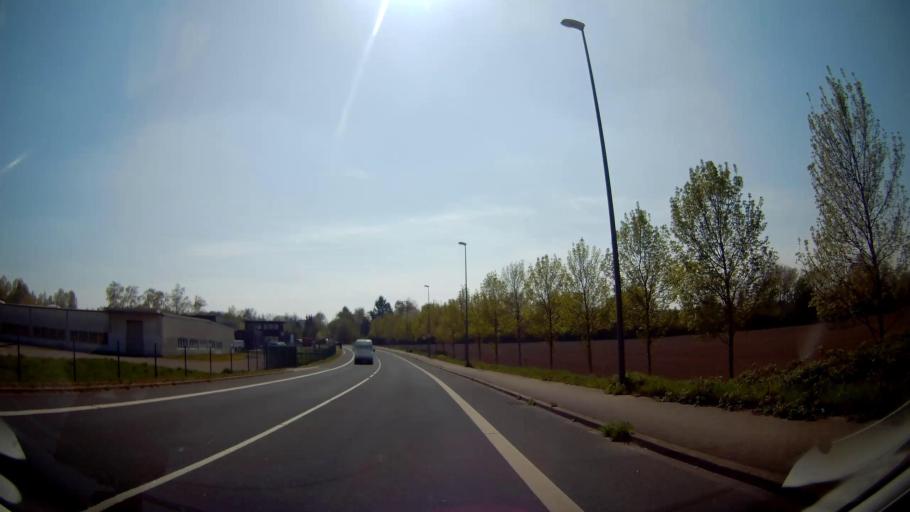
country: DE
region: North Rhine-Westphalia
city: Bochum-Hordel
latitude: 51.4915
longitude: 7.1593
